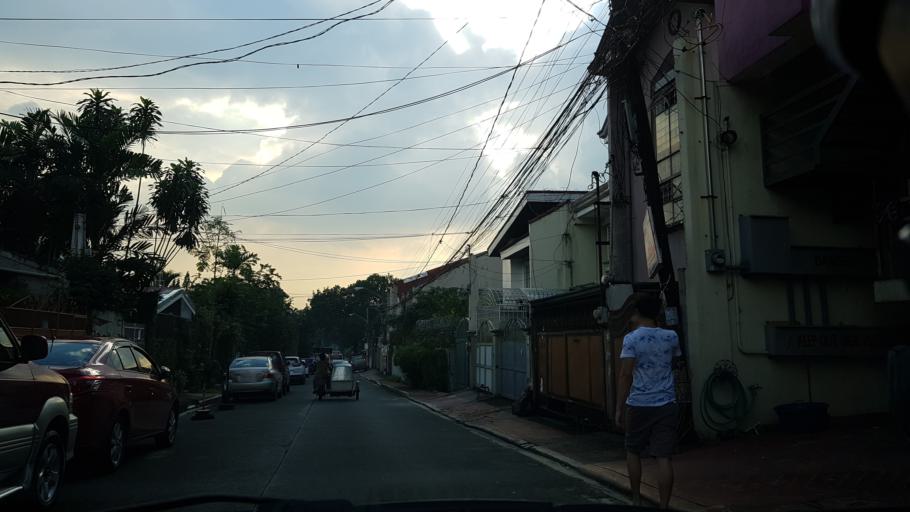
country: PH
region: Metro Manila
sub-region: Quezon City
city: Quezon City
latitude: 14.6334
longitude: 121.0584
